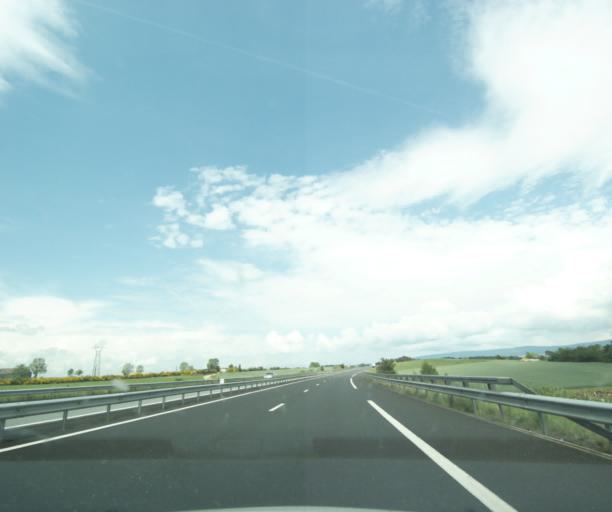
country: FR
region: Languedoc-Roussillon
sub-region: Departement de la Lozere
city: Le Malzieu-Ville
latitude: 44.8982
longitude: 3.2299
